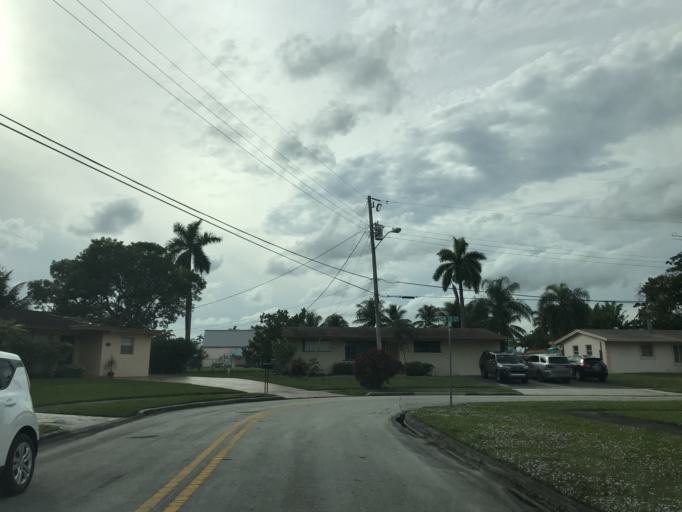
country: US
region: Florida
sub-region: Broward County
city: Margate
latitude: 26.2537
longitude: -80.2079
